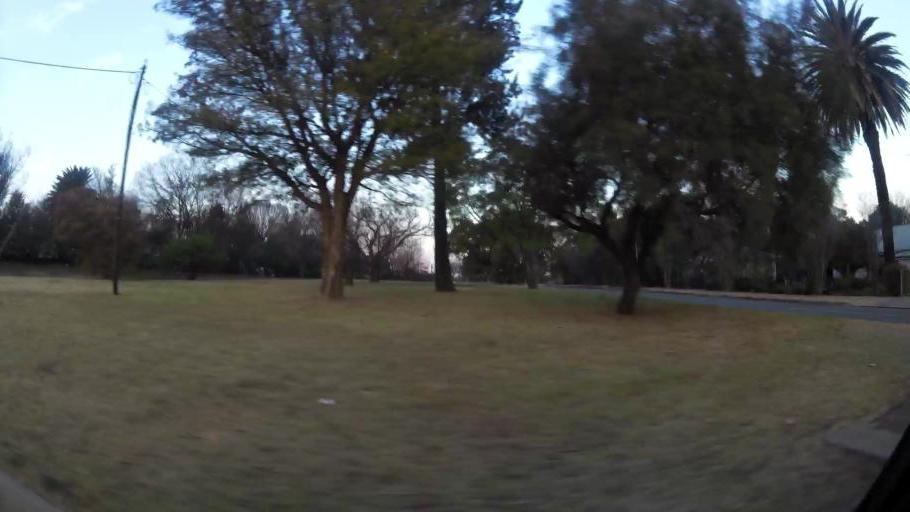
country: ZA
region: Gauteng
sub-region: City of Johannesburg Metropolitan Municipality
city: Diepsloot
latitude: -26.0047
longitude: 28.0445
